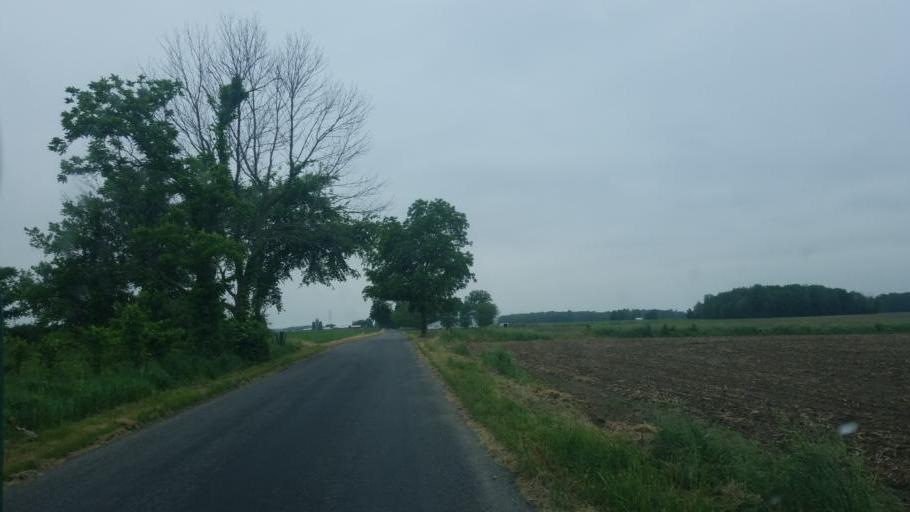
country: US
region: Indiana
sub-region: Marshall County
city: Bremen
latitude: 41.4937
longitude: -86.1220
